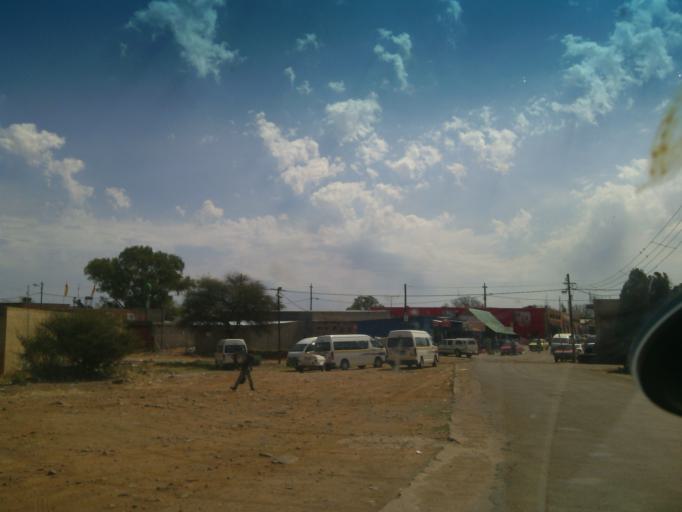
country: ZA
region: Northern Cape
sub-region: Frances Baard District Municipality
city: Barkly West
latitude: -28.5393
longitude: 24.5181
